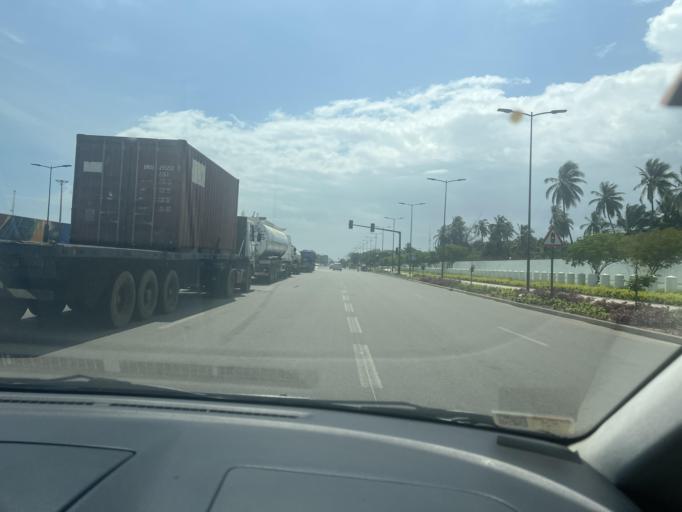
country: BJ
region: Littoral
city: Cotonou
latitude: 6.3506
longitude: 2.4149
